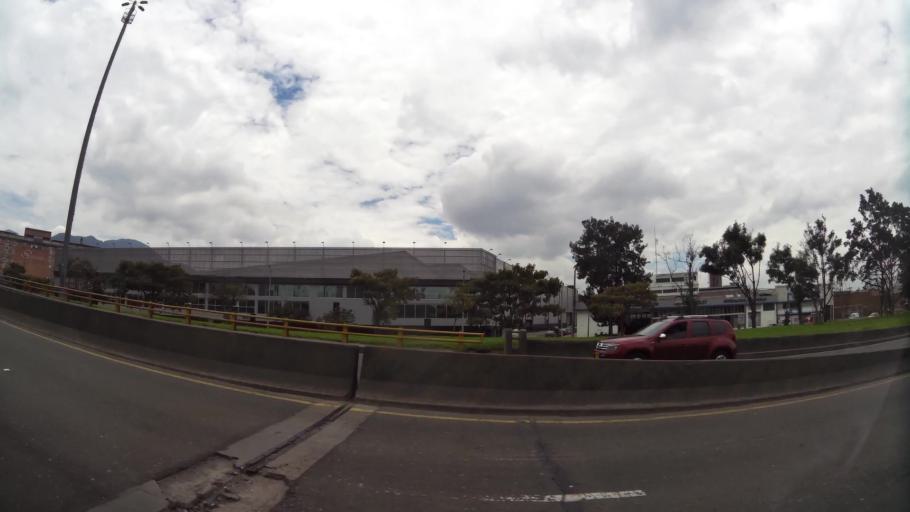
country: CO
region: Bogota D.C.
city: Bogota
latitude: 4.6251
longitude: -74.0847
